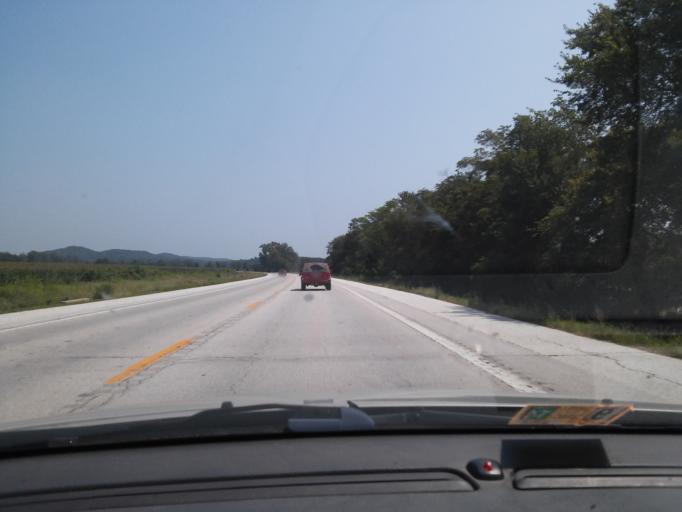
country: US
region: Missouri
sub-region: Pike County
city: Bowling Green
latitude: 39.3837
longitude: -91.1284
